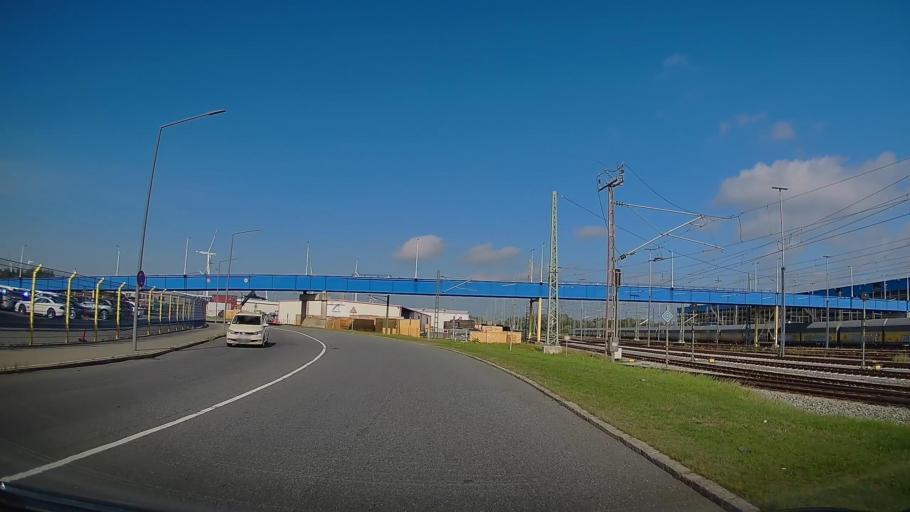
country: DE
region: Bremen
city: Bremerhaven
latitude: 53.5769
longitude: 8.5623
